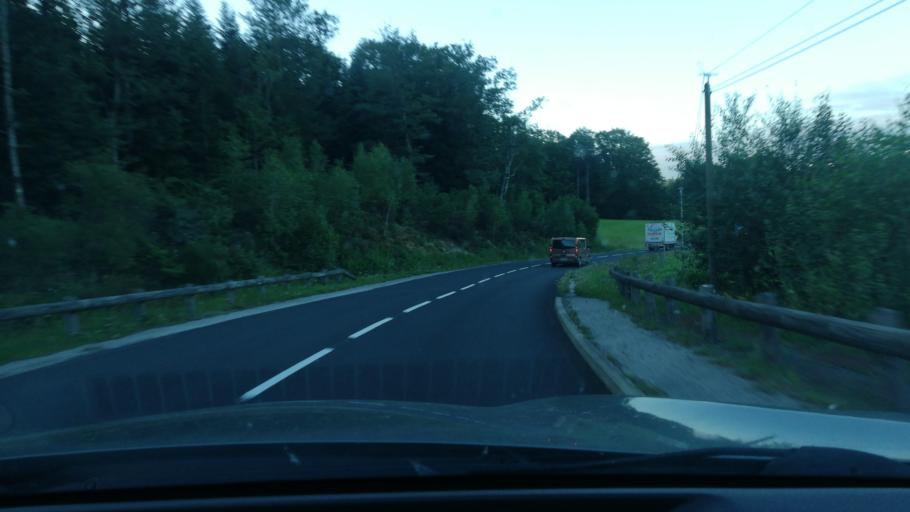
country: FR
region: Auvergne
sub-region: Departement du Cantal
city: Laroquebrou
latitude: 44.9267
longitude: 2.0751
